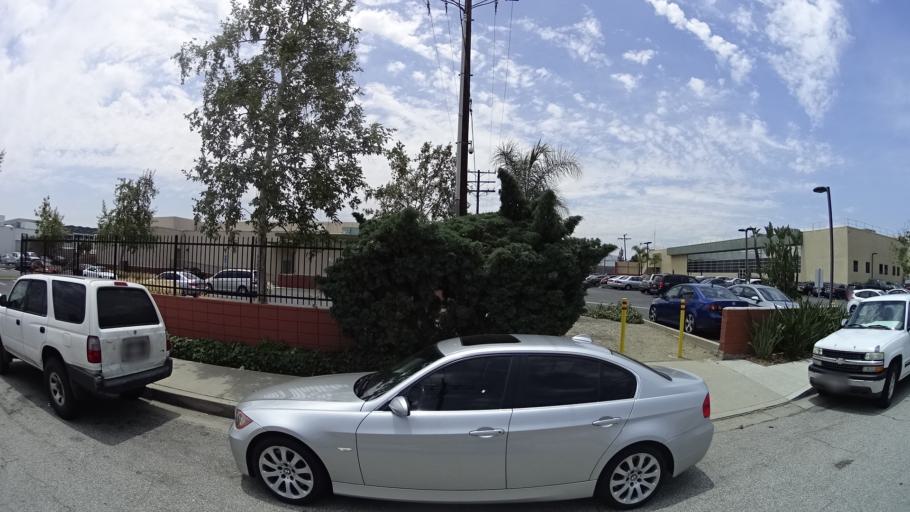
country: US
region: California
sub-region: Los Angeles County
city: North Glendale
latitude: 34.1643
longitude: -118.2885
